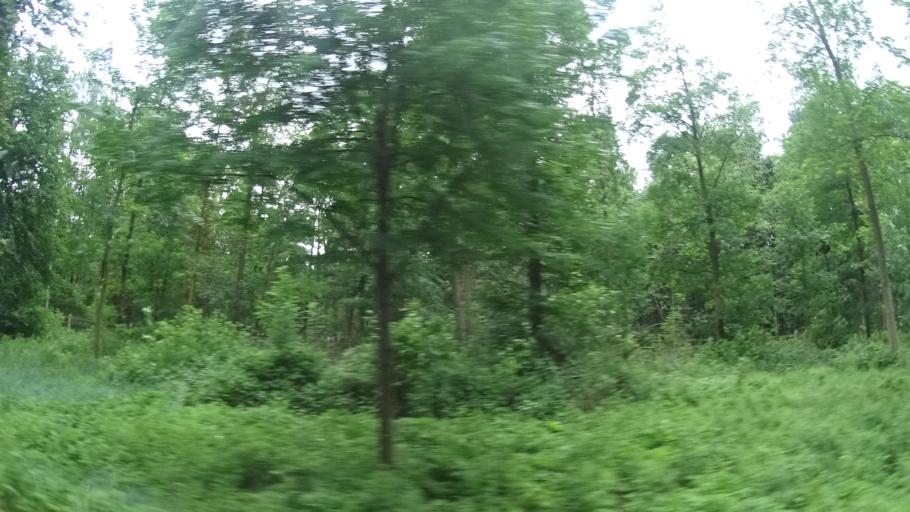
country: DE
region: Lower Saxony
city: Springe
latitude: 52.1792
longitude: 9.5961
